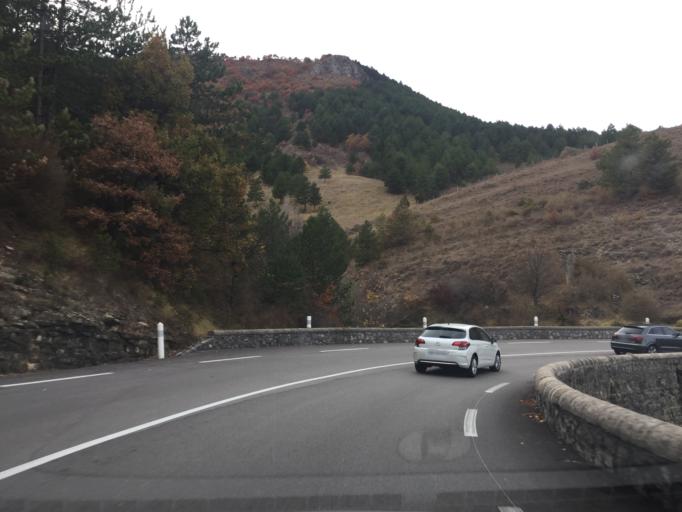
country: FR
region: Rhone-Alpes
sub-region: Departement de l'Ardeche
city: Saint-Priest
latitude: 44.7276
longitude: 4.5396
